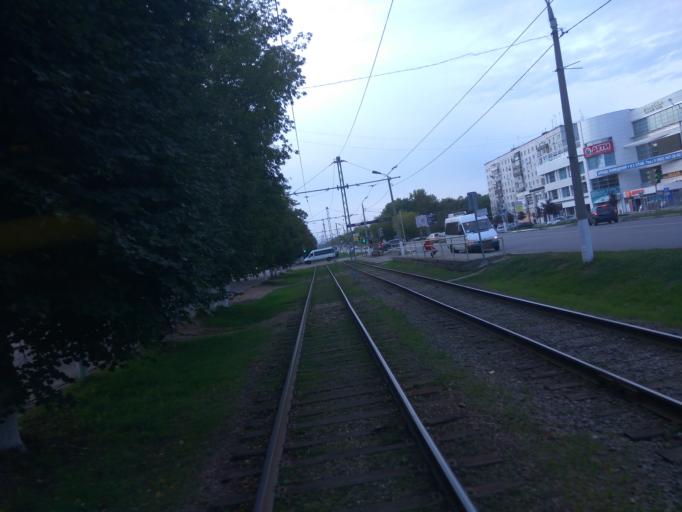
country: RU
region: Moskovskaya
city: Kolomna
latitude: 55.0859
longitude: 38.7965
